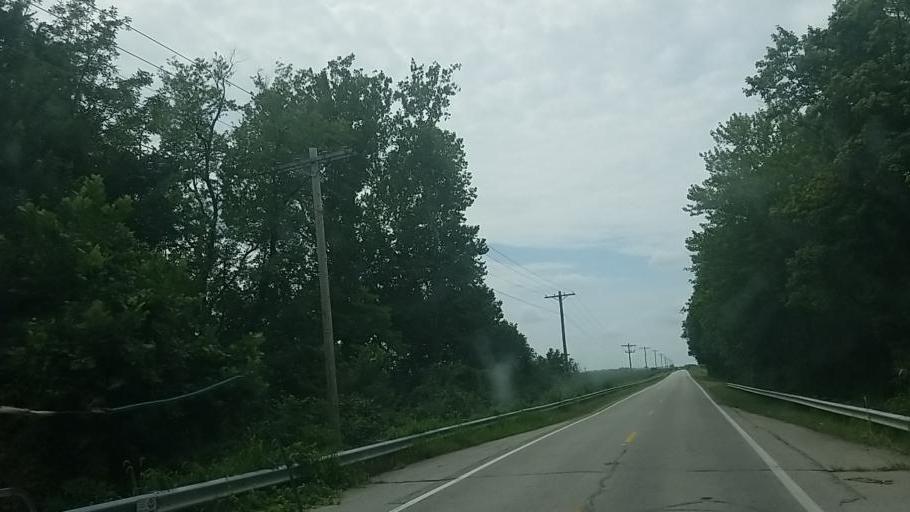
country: US
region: Ohio
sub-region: Franklin County
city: Groveport
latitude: 39.8280
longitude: -82.8916
